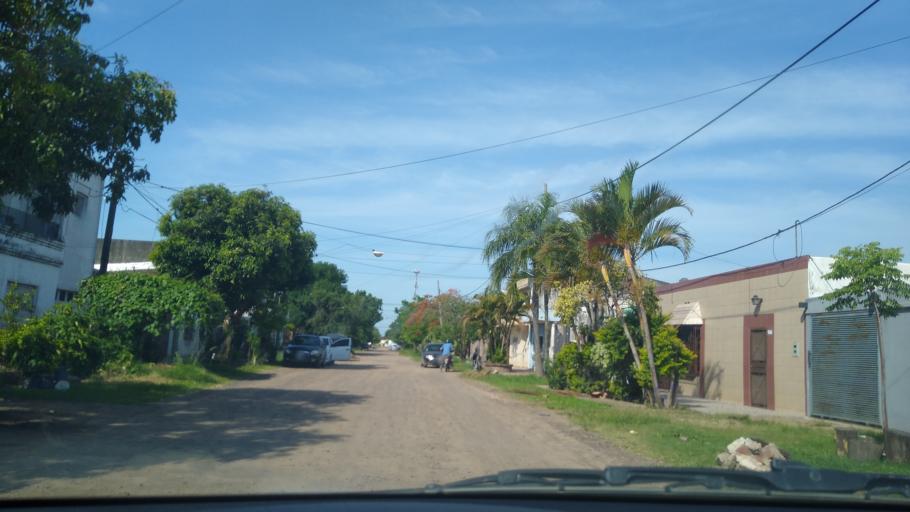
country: AR
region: Chaco
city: Barranqueras
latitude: -27.4869
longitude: -58.9458
